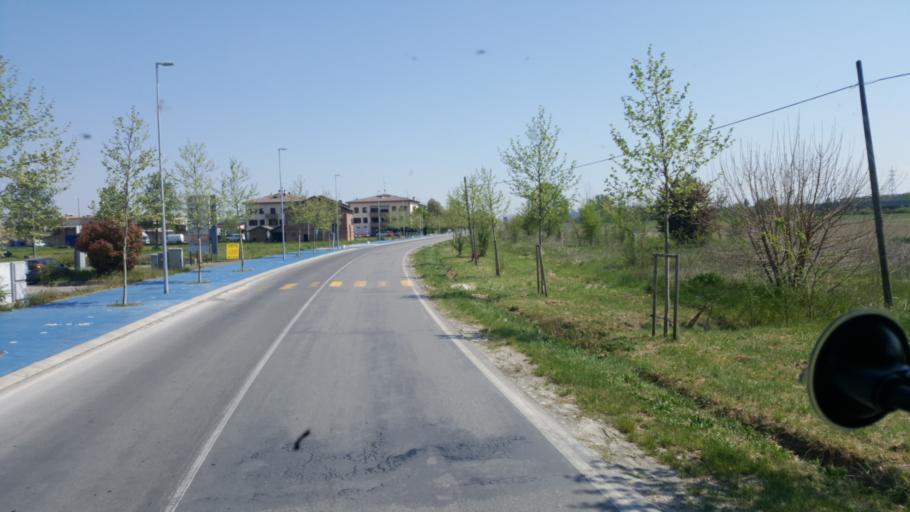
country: IT
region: Emilia-Romagna
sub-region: Provincia di Reggio Emilia
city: Reggio nell'Emilia
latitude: 44.7304
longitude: 10.6437
